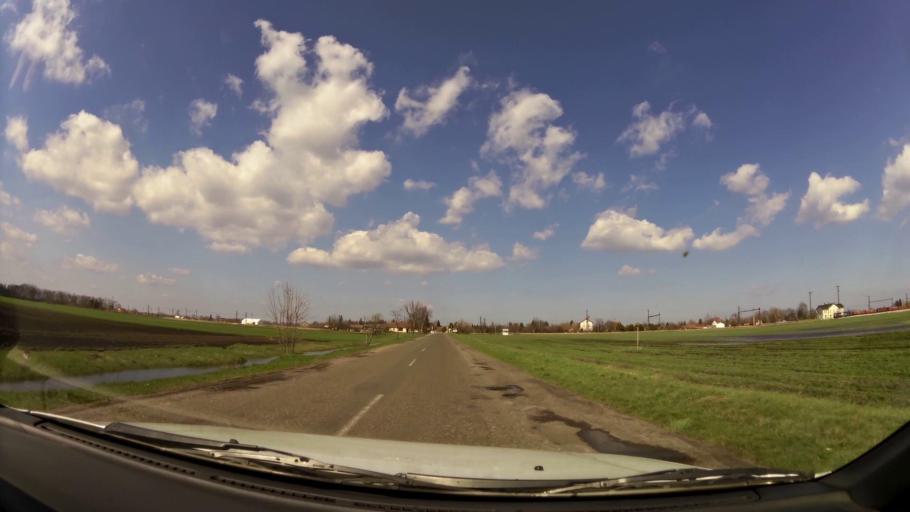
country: HU
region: Pest
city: Tapiogyorgye
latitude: 47.3232
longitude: 19.9462
